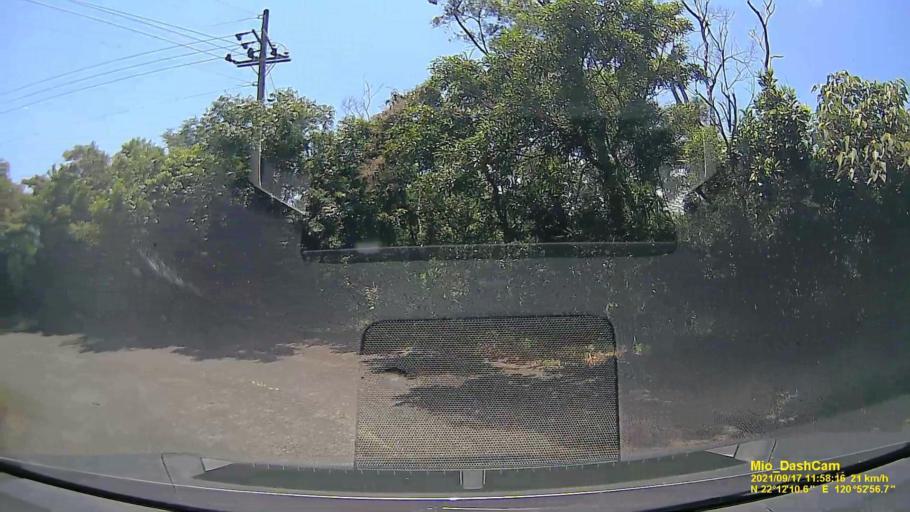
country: TW
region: Taiwan
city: Hengchun
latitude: 22.2030
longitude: 120.8825
